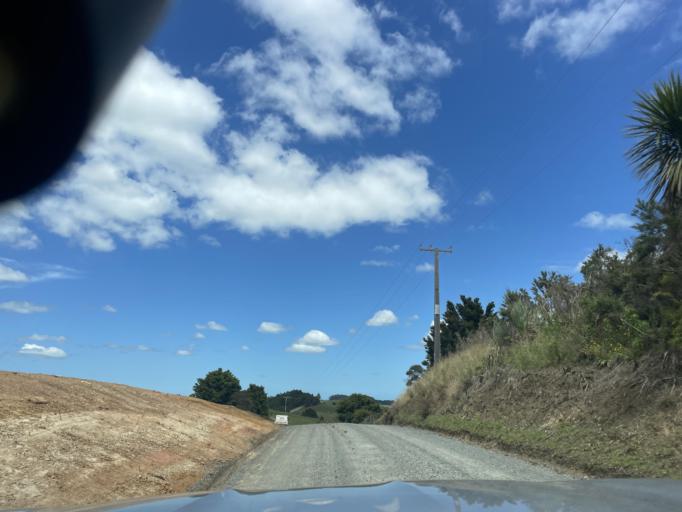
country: NZ
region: Auckland
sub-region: Auckland
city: Wellsford
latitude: -36.1573
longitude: 174.5398
